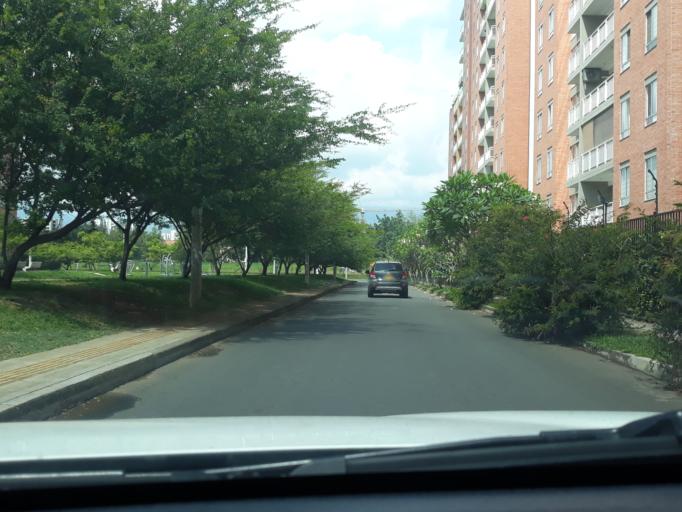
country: CO
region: Valle del Cauca
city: Cali
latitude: 3.3697
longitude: -76.5107
